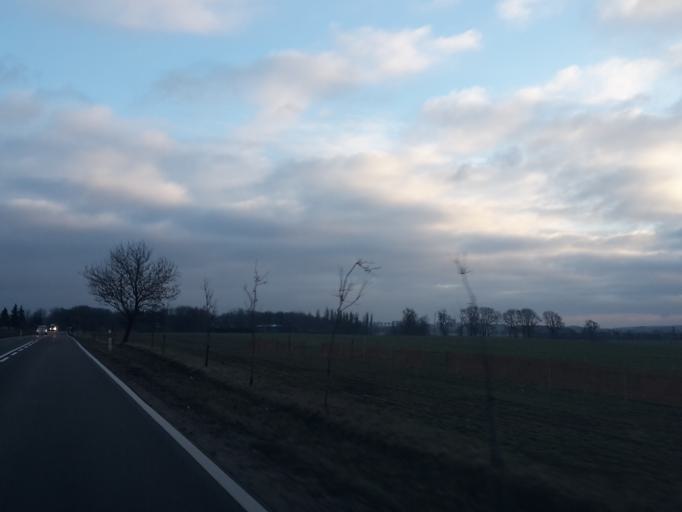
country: PL
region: Warmian-Masurian Voivodeship
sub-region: Powiat ilawski
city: Lubawa
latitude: 53.5913
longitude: 19.8493
